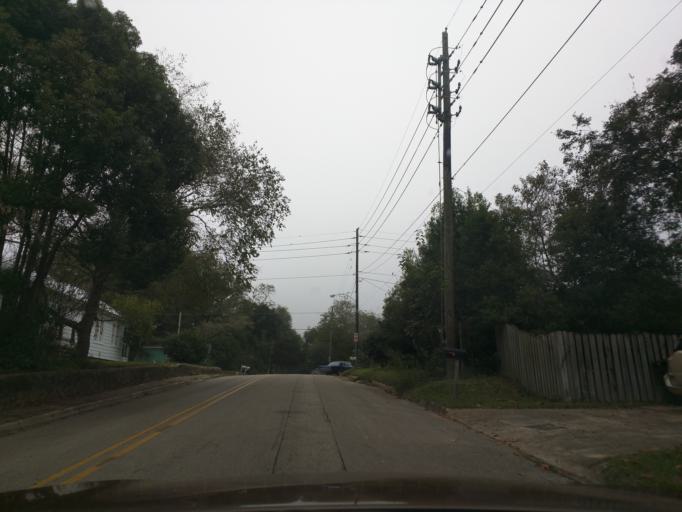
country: US
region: Florida
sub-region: Leon County
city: Tallahassee
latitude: 30.4578
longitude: -84.2880
